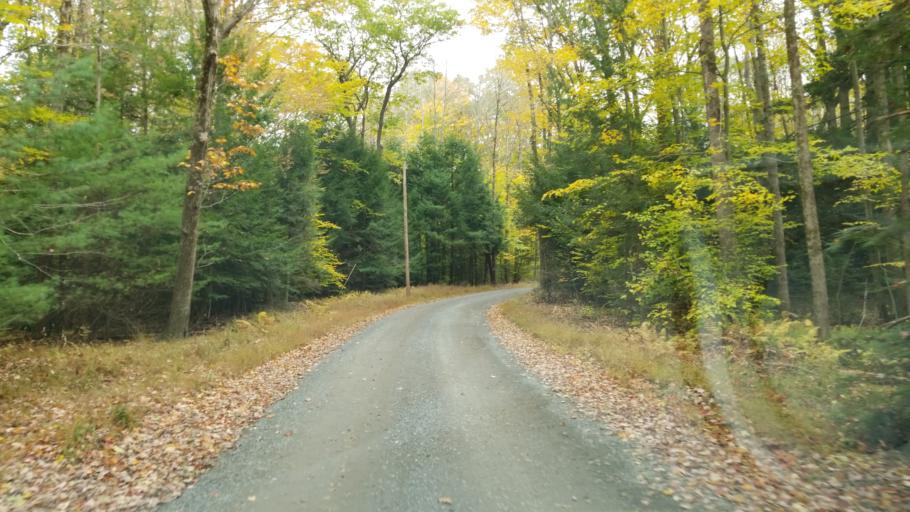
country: US
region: Pennsylvania
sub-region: Clearfield County
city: Clearfield
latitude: 41.1984
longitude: -78.4141
